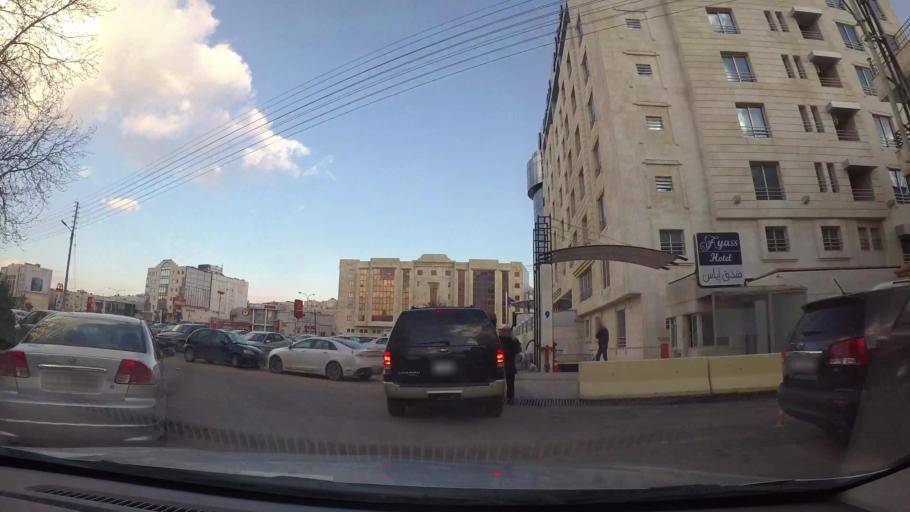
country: JO
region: Amman
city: Al Jubayhah
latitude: 31.9826
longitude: 35.8639
